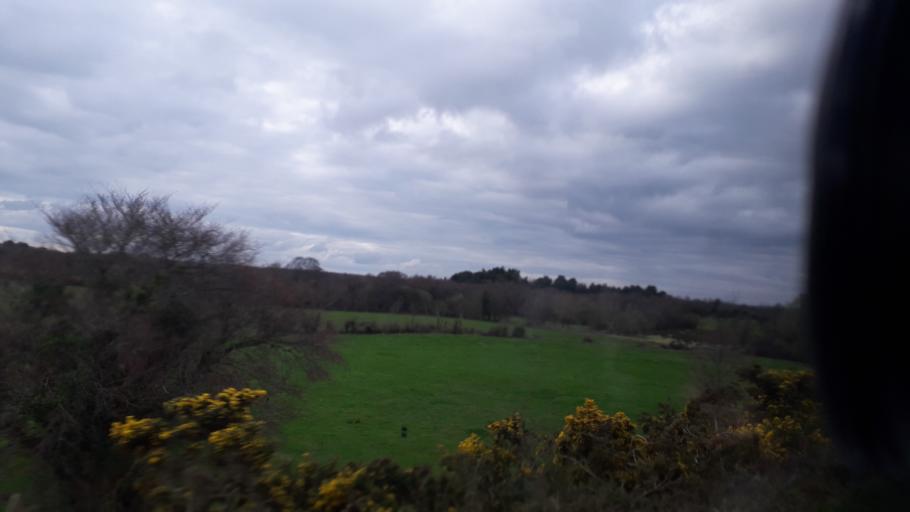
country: IE
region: Leinster
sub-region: An Iarmhi
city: Castlepollard
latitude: 53.6422
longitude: -7.4210
